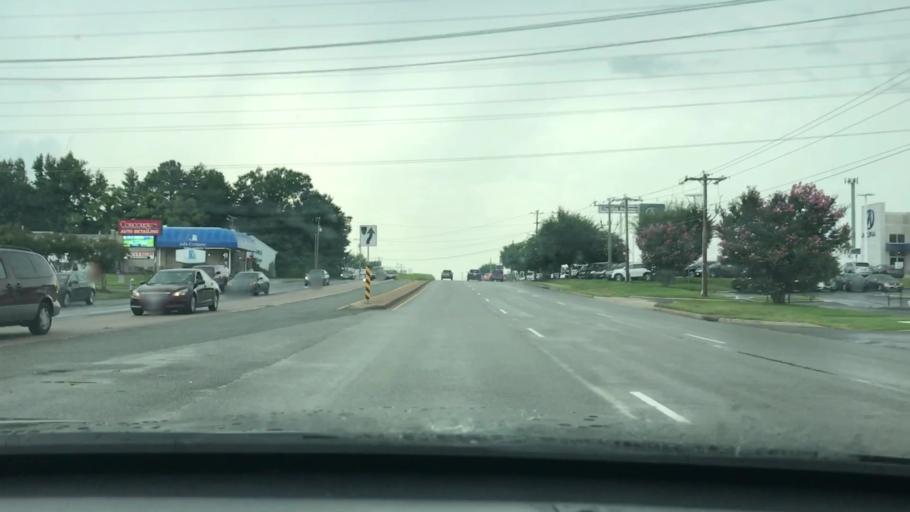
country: US
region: Virginia
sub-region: Henrico County
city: Laurel
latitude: 37.6326
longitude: -77.5402
